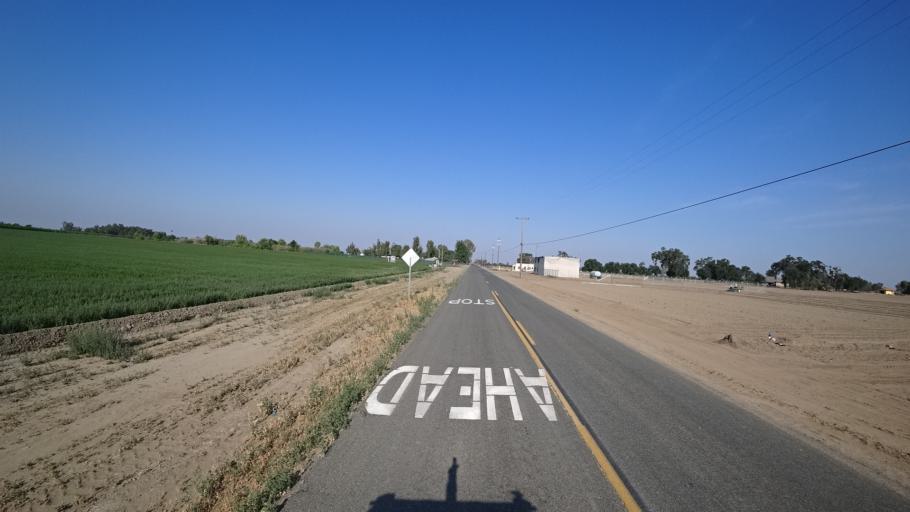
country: US
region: California
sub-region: Fresno County
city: Riverdale
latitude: 36.3585
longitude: -119.8530
